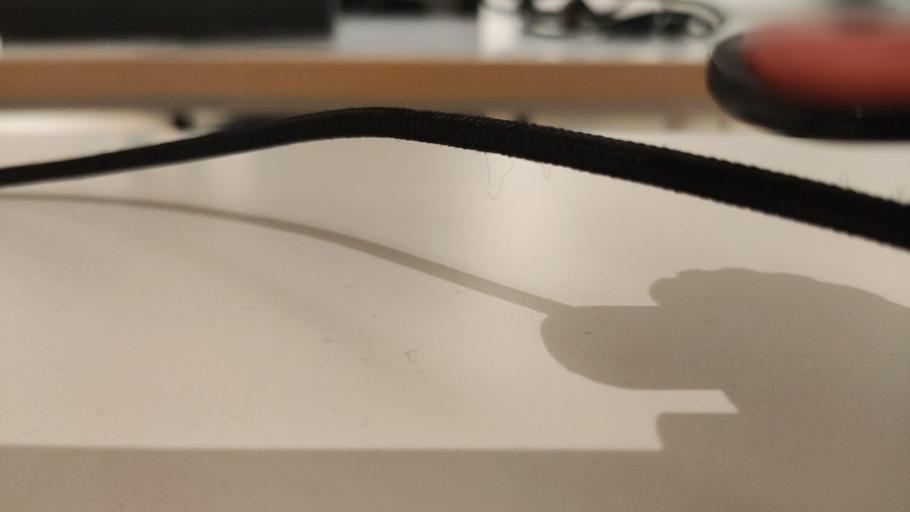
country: RU
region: Moskovskaya
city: Dorokhovo
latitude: 55.3817
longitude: 36.4005
